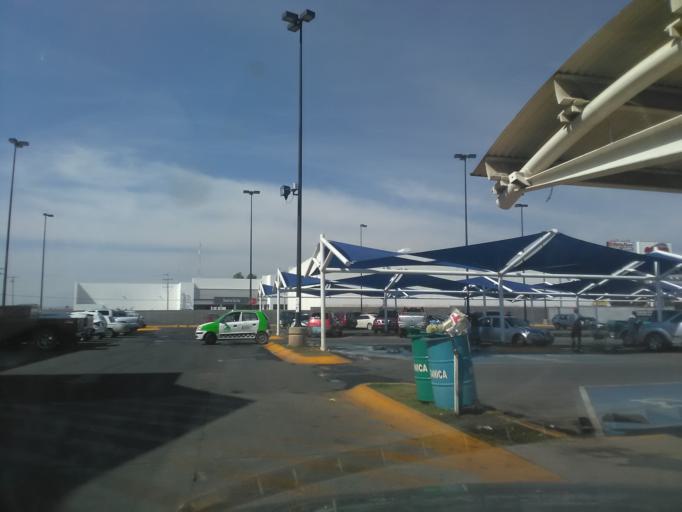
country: MX
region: Durango
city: Victoria de Durango
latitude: 24.0562
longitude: -104.6120
